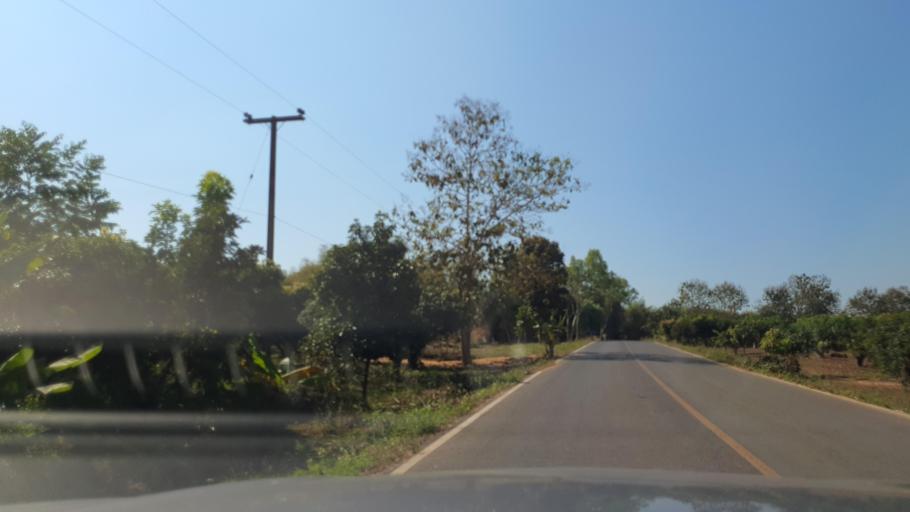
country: TH
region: Nan
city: Pua
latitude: 19.1236
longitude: 100.9207
